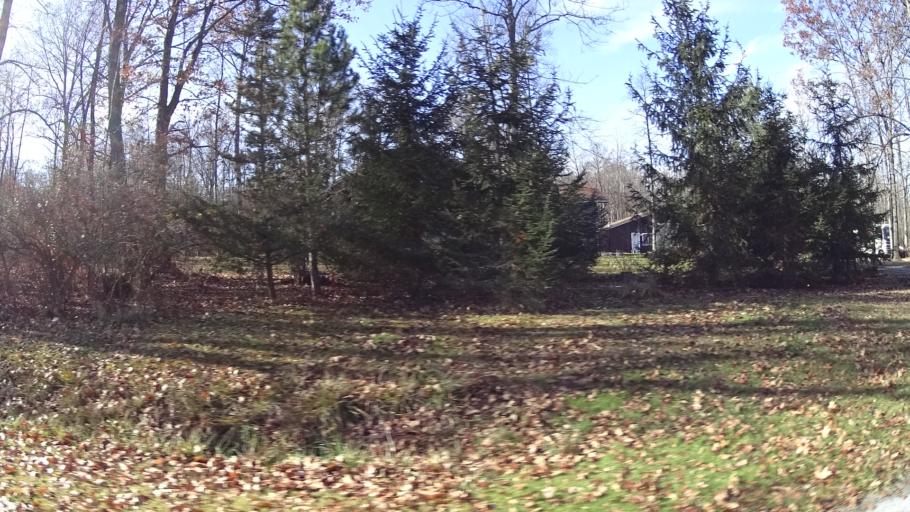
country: US
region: Ohio
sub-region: Lorain County
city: Wellington
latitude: 41.0645
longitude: -82.2017
